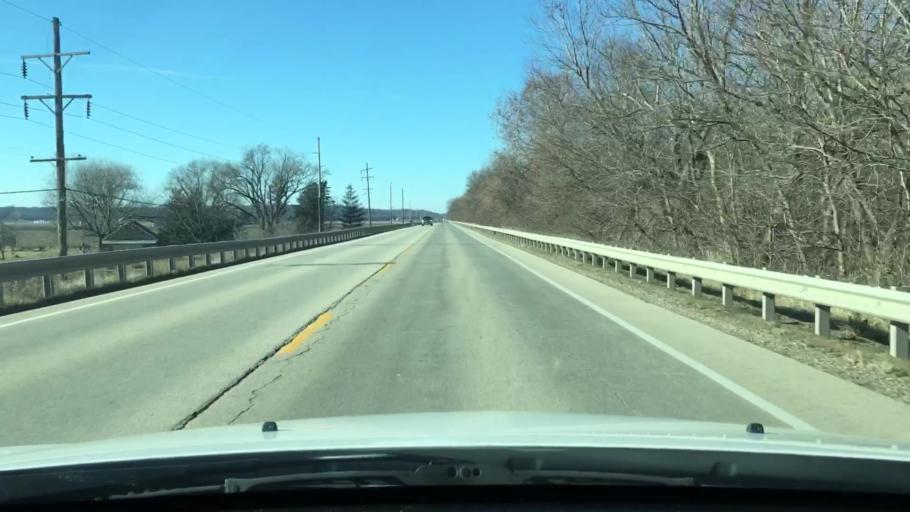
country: US
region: Illinois
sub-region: Mason County
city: Havana
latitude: 40.2981
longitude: -90.0937
